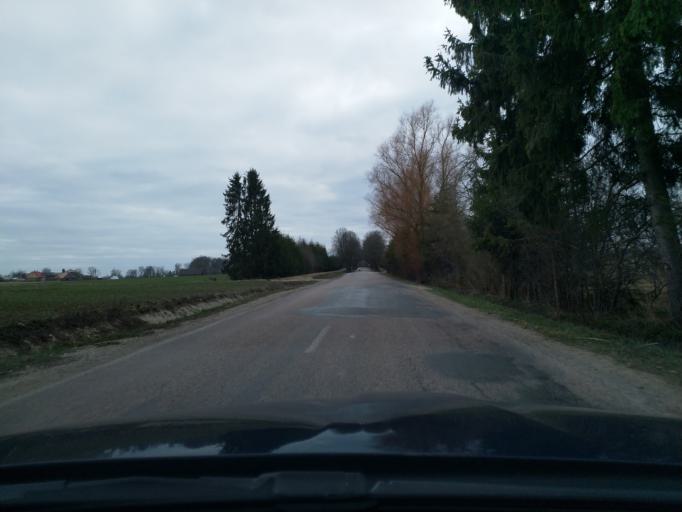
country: LV
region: Talsu Rajons
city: Sabile
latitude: 56.9304
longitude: 22.5668
